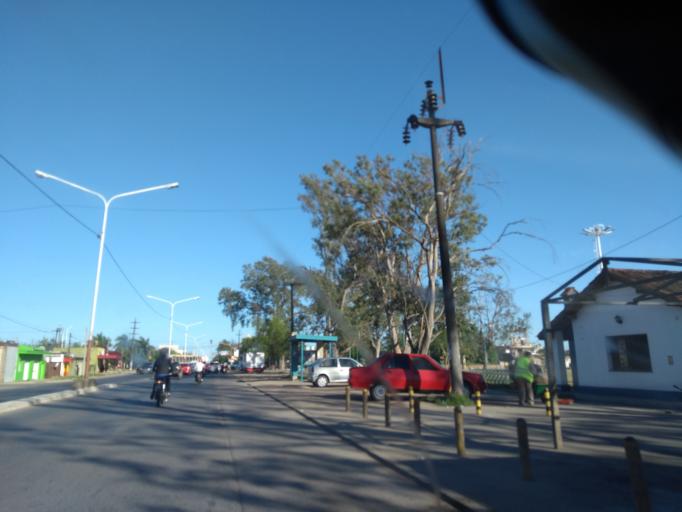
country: AR
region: Chaco
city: Resistencia
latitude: -27.4710
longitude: -58.9783
